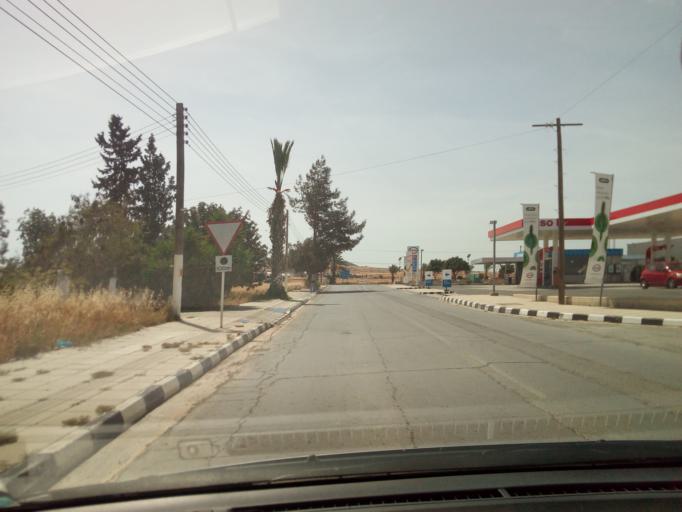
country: CY
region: Larnaka
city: Athienou
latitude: 35.0555
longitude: 33.5333
